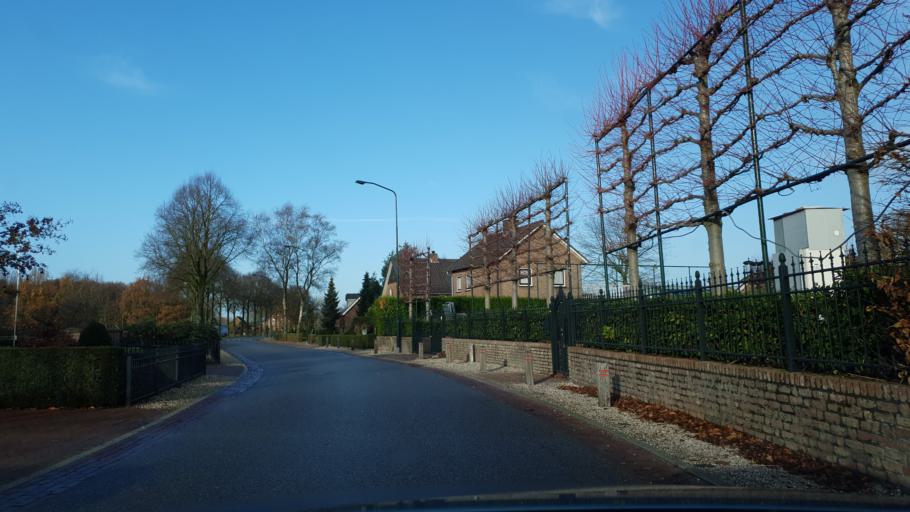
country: NL
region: Gelderland
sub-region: Gemeente Wijchen
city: Bergharen
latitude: 51.8363
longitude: 5.6803
